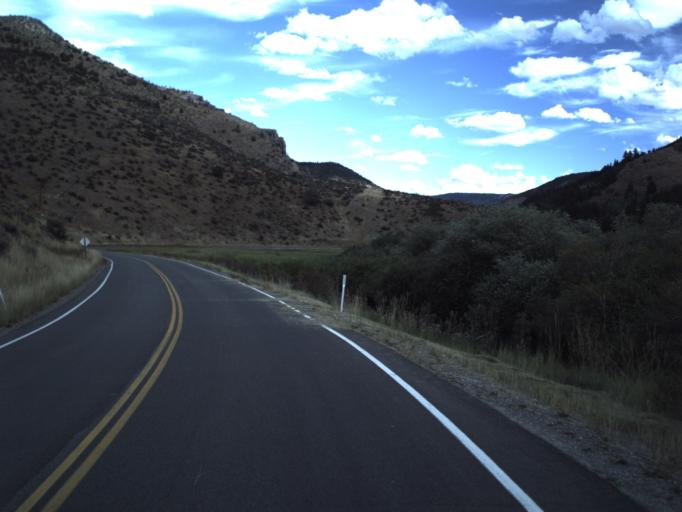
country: US
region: Utah
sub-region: Cache County
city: Millville
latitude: 41.6229
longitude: -111.6678
